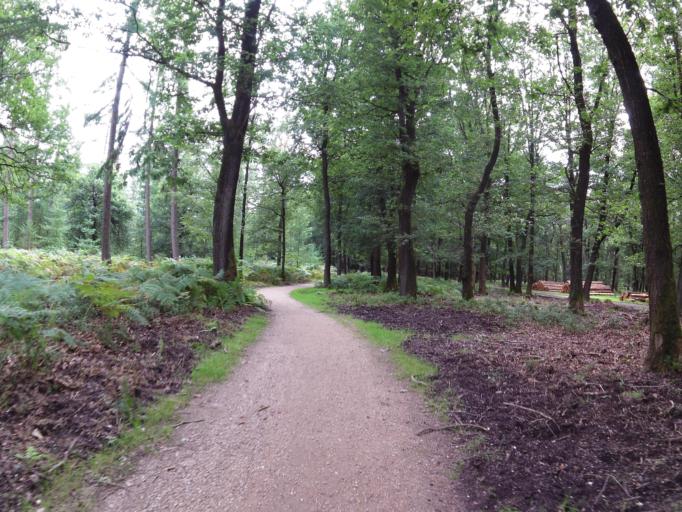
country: NL
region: Gelderland
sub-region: Gemeente Apeldoorn
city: Loenen
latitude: 52.0940
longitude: 5.9906
